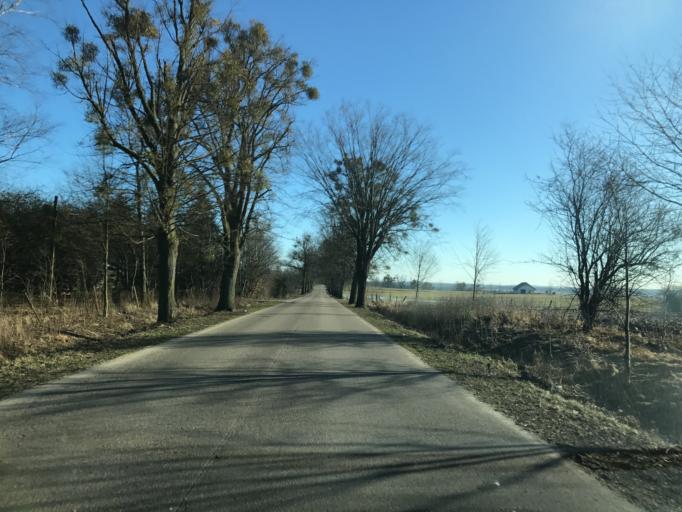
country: PL
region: Warmian-Masurian Voivodeship
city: Dobre Miasto
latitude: 53.9632
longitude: 20.3633
